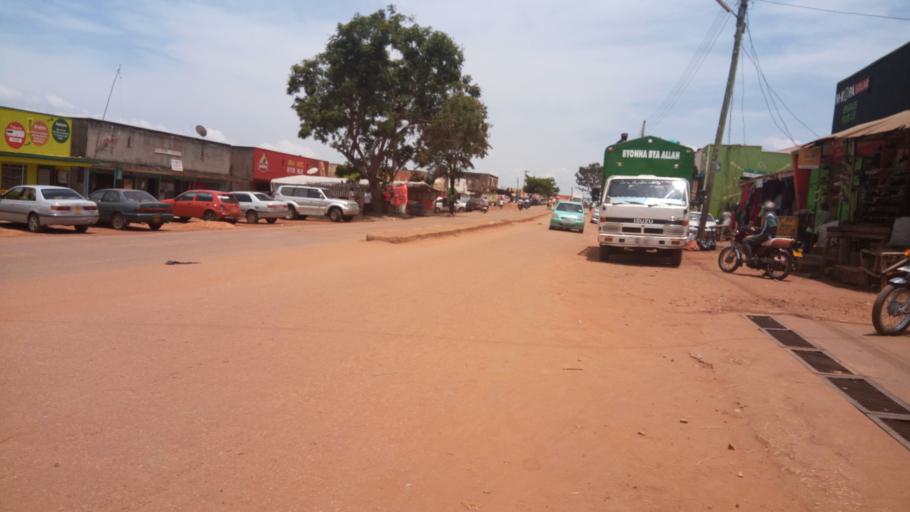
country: UG
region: Central Region
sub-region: Mityana District
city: Mityana
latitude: 0.3996
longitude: 32.0451
